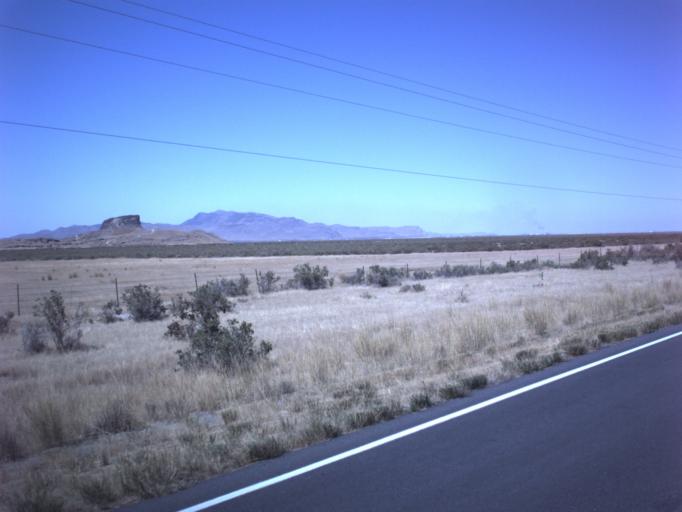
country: US
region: Utah
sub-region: Tooele County
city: Grantsville
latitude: 40.6932
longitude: -112.6677
